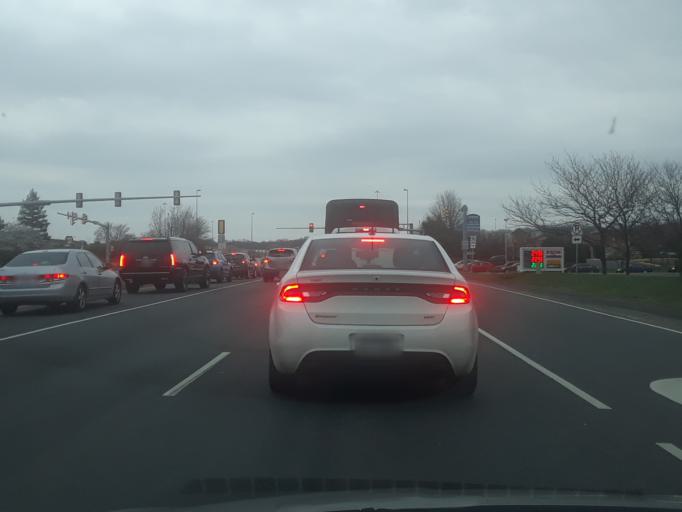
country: US
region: Virginia
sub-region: Loudoun County
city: Sterling
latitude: 38.9791
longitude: -77.4356
